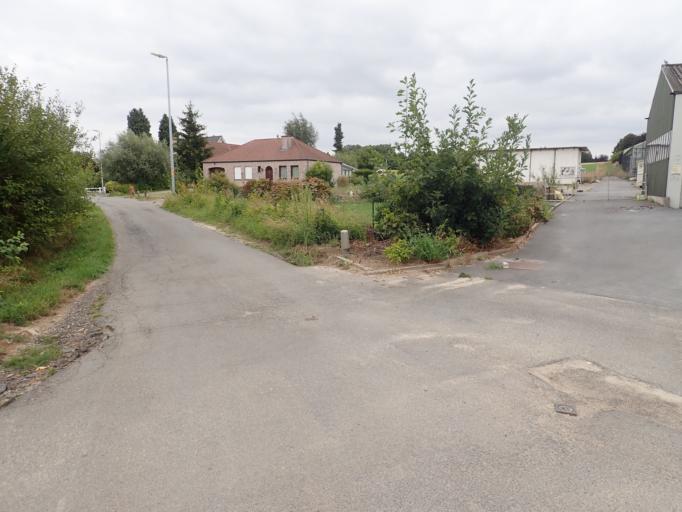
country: BE
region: Flanders
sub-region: Provincie Oost-Vlaanderen
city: Denderleeuw
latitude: 50.9106
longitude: 4.1175
